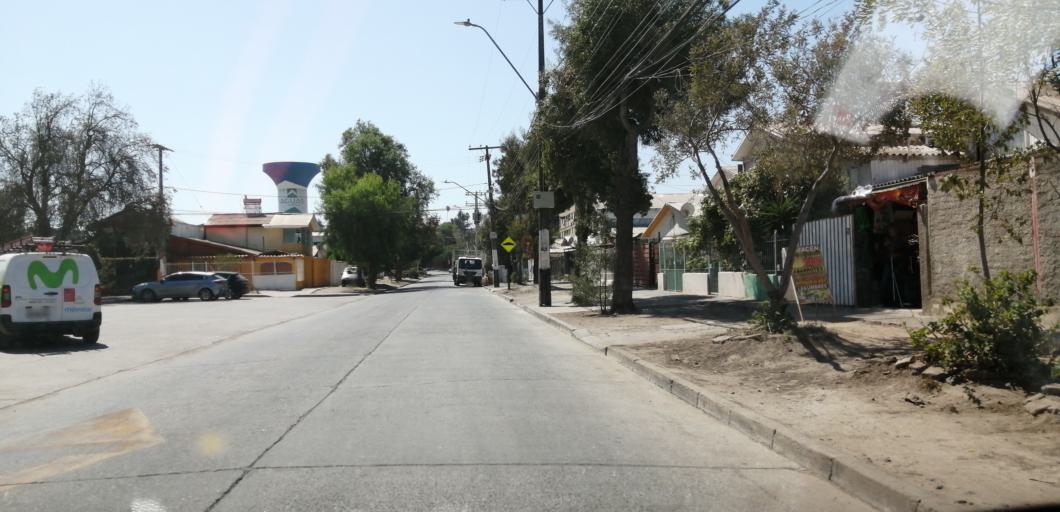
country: CL
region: Santiago Metropolitan
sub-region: Provincia de Santiago
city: Lo Prado
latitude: -33.4500
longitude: -70.7448
